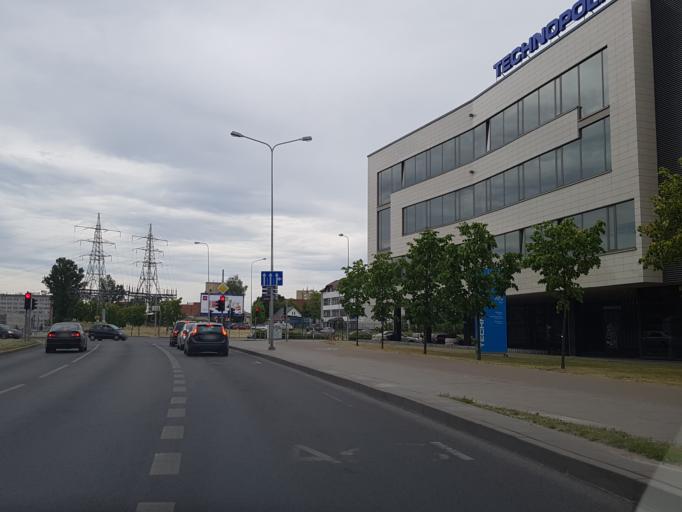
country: LT
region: Vilnius County
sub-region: Vilnius
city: Vilnius
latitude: 54.7179
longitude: 25.2865
